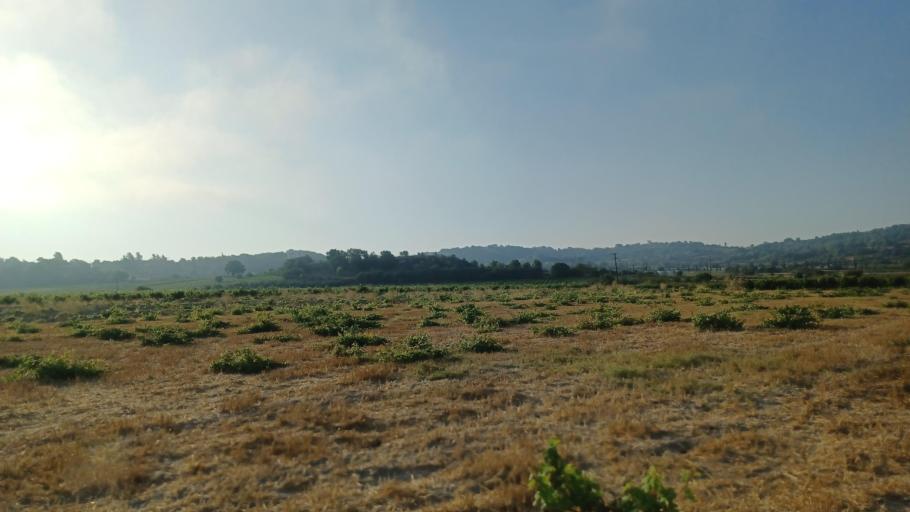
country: CY
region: Pafos
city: Tala
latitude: 34.8895
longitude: 32.4936
